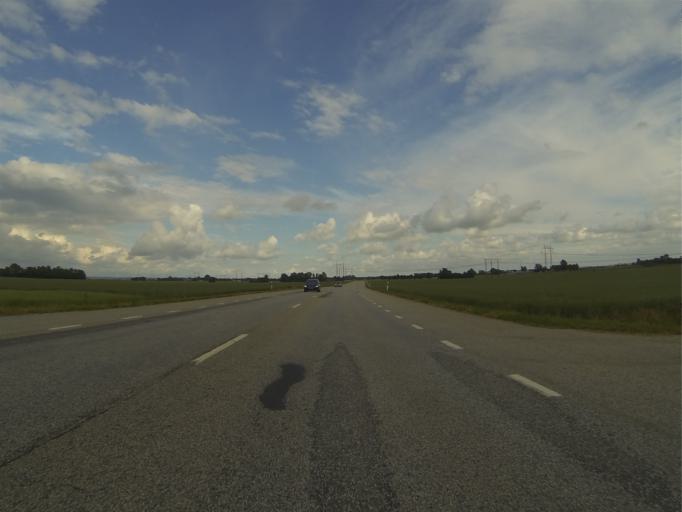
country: SE
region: Skane
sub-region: Staffanstorps Kommun
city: Hjaerup
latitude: 55.6418
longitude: 13.1594
